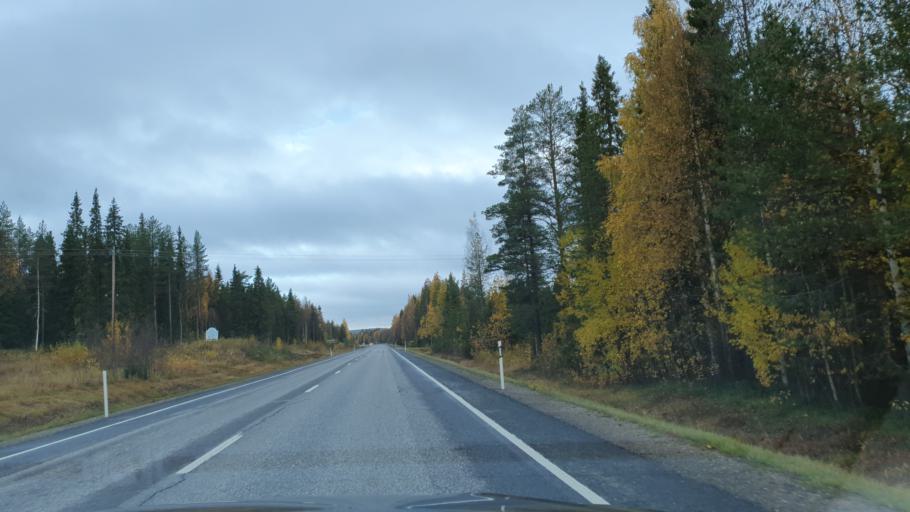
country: FI
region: Lapland
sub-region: Rovaniemi
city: Rovaniemi
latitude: 66.5680
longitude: 25.6376
